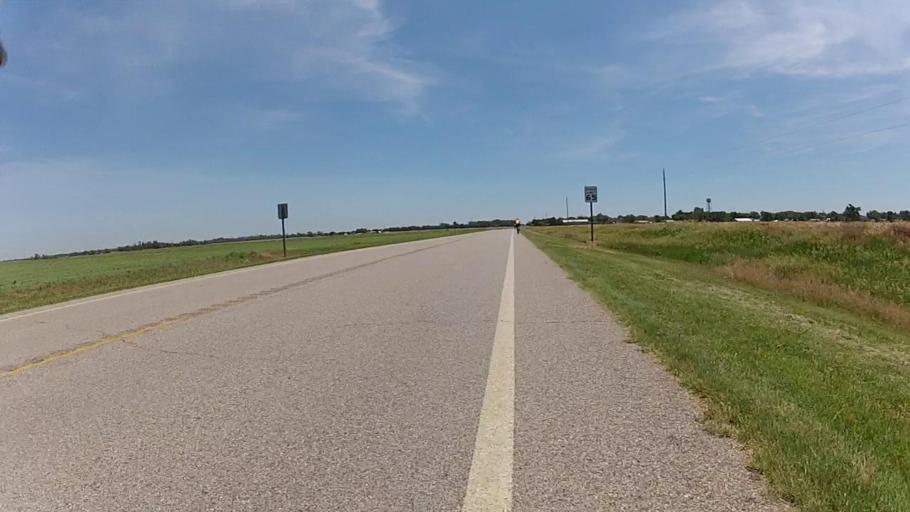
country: US
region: Kansas
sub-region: Barber County
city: Medicine Lodge
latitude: 37.2535
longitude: -98.4270
